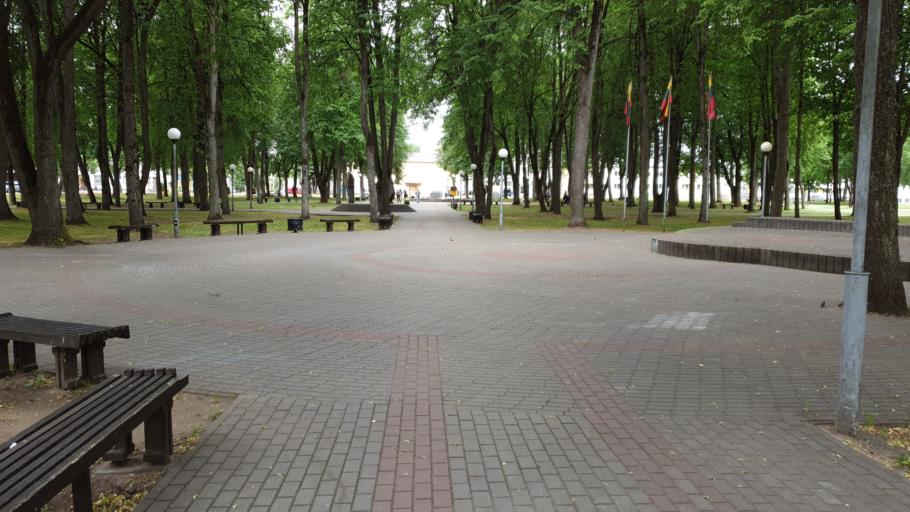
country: LT
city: Svencionys
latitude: 55.1348
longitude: 26.1590
